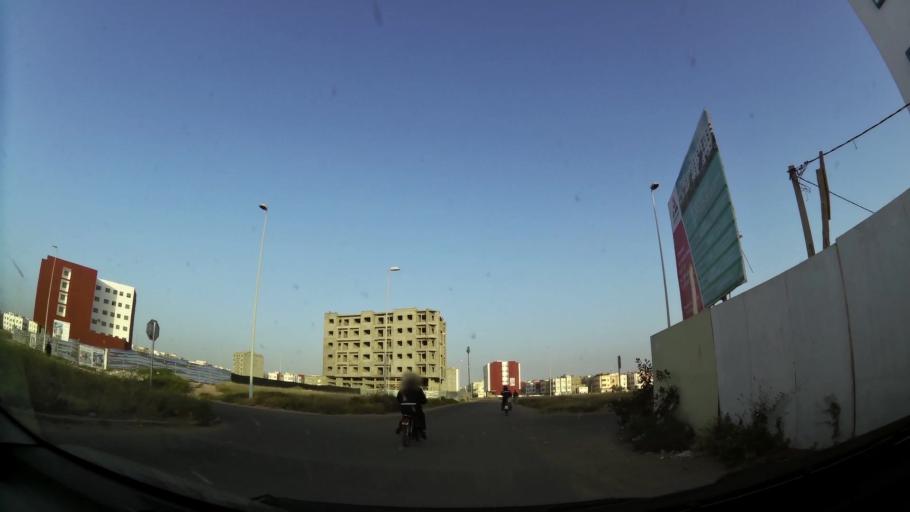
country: MA
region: Oued ed Dahab-Lagouira
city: Dakhla
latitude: 30.4001
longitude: -9.5660
